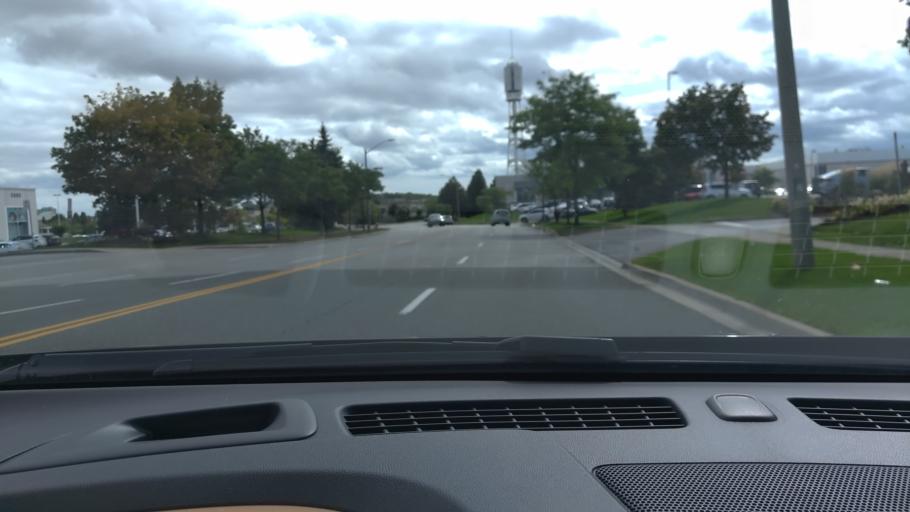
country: CA
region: Ontario
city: Mississauga
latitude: 43.6143
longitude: -79.6919
